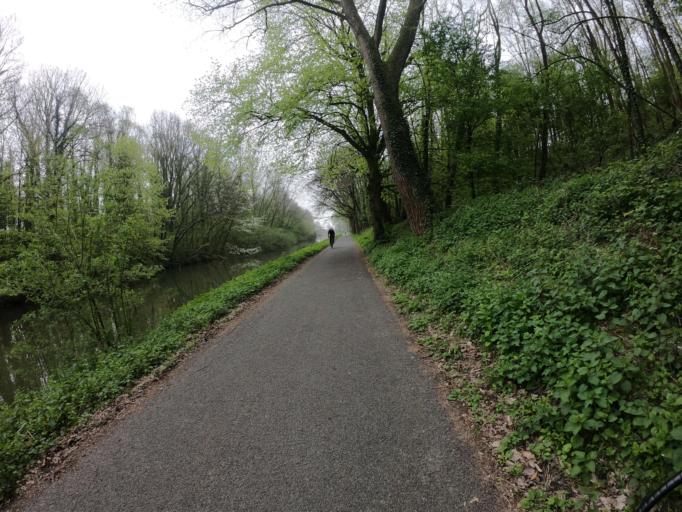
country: BE
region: Flanders
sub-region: Provincie West-Vlaanderen
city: Zwevegem
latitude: 50.7806
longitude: 3.3778
